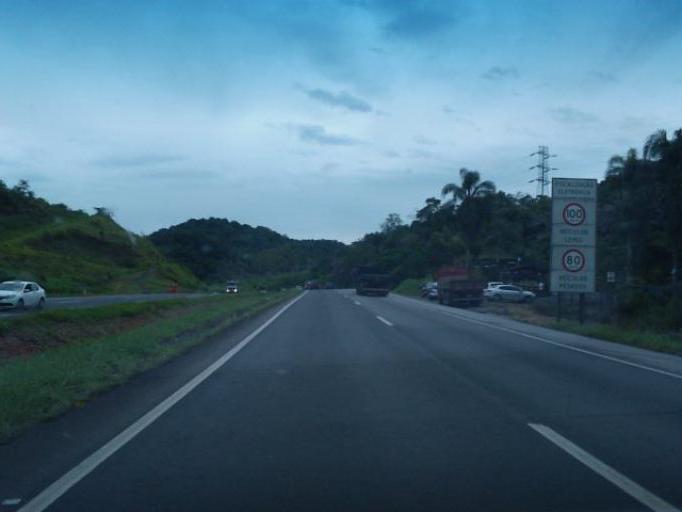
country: BR
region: Sao Paulo
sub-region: Juquia
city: Juquia
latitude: -24.3709
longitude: -47.7035
